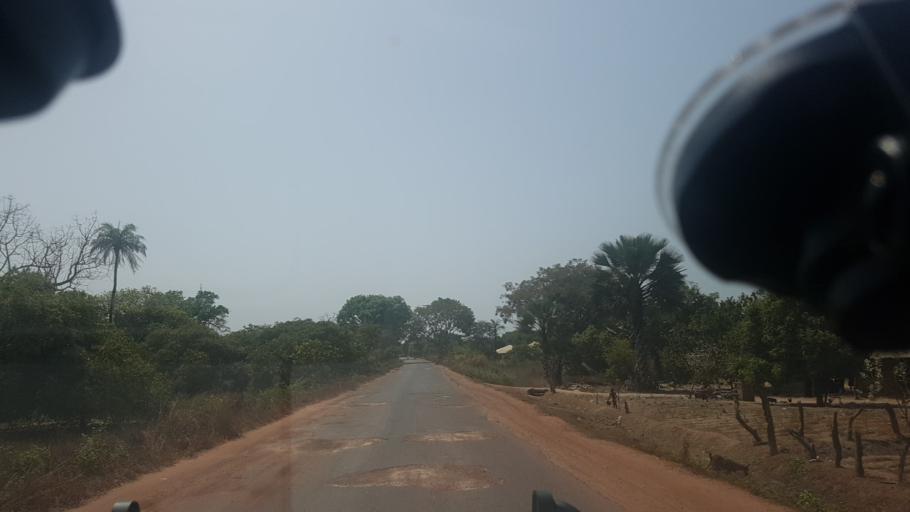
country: GW
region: Cacheu
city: Cacheu
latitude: 12.4095
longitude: -16.0424
